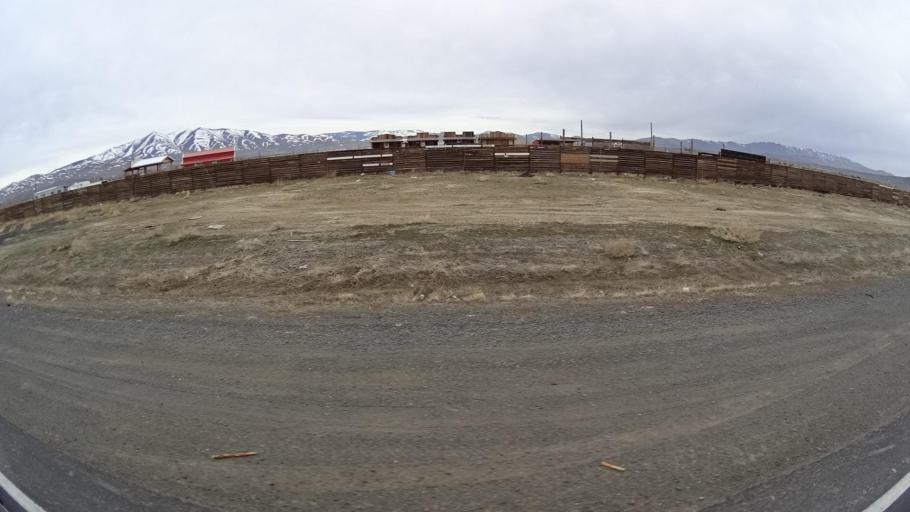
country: US
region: Nevada
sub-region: Washoe County
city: Lemmon Valley
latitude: 39.6518
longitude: -119.8286
